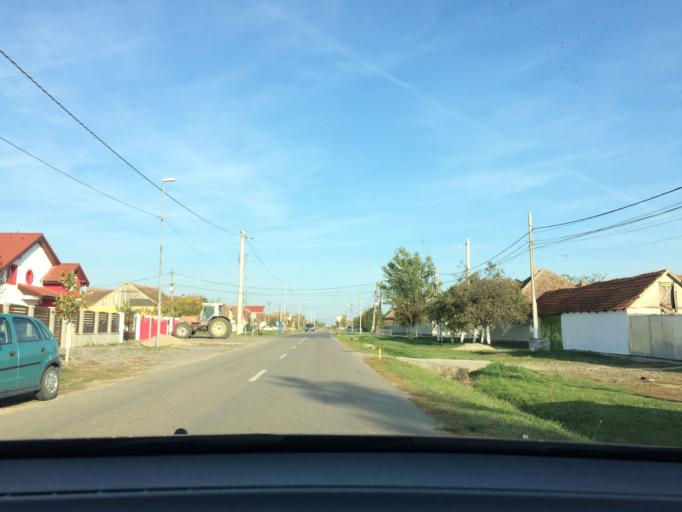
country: RO
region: Timis
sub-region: Oras Recas
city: Recas
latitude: 45.8059
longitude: 21.5126
